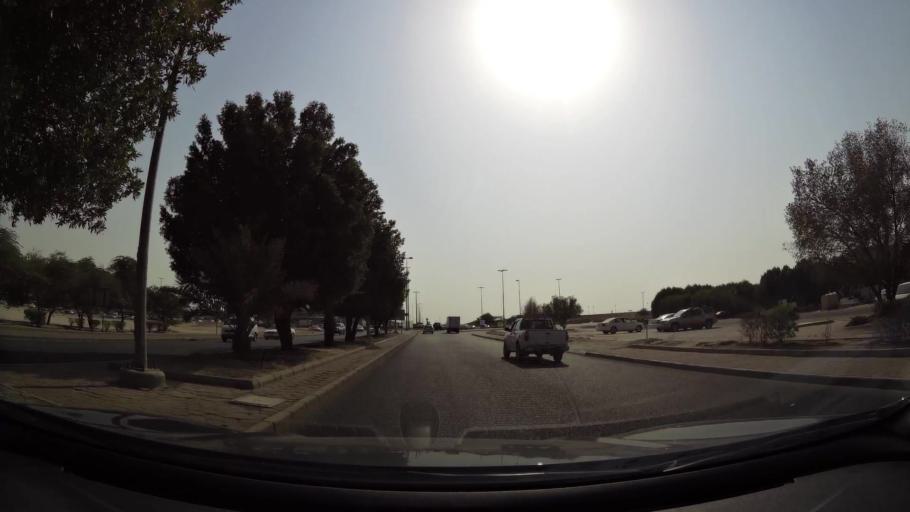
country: KW
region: Muhafazat al Jahra'
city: Al Jahra'
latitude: 29.3207
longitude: 47.6595
